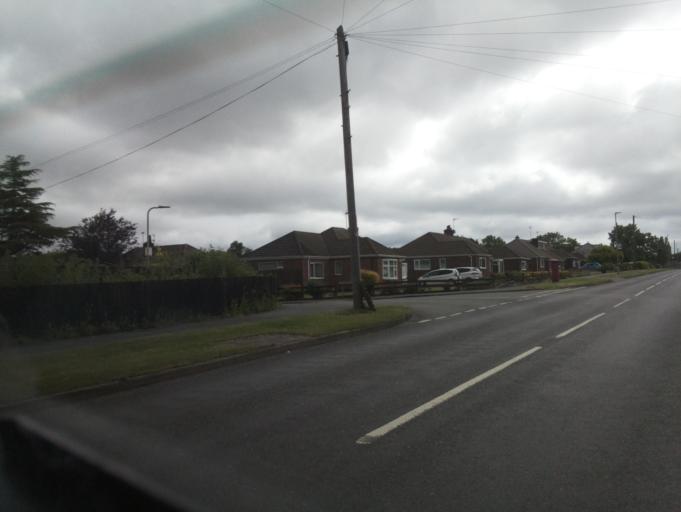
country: GB
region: England
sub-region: Leicestershire
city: Coalville
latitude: 52.7314
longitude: -1.3479
